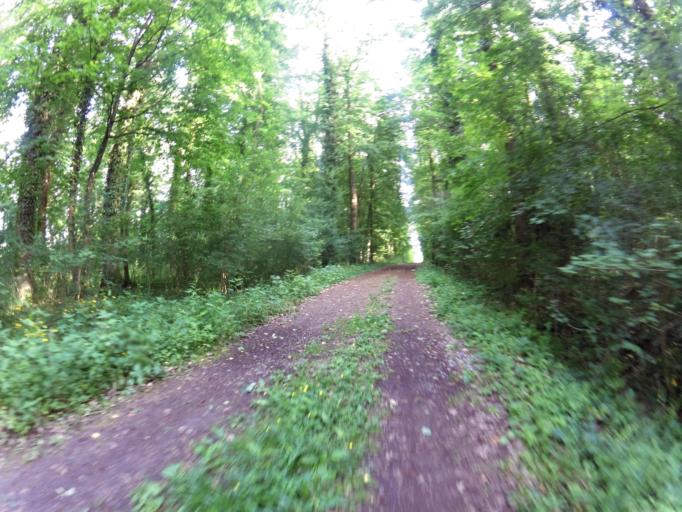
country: DE
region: Bavaria
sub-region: Regierungsbezirk Unterfranken
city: Ochsenfurt
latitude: 49.6814
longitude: 10.0722
